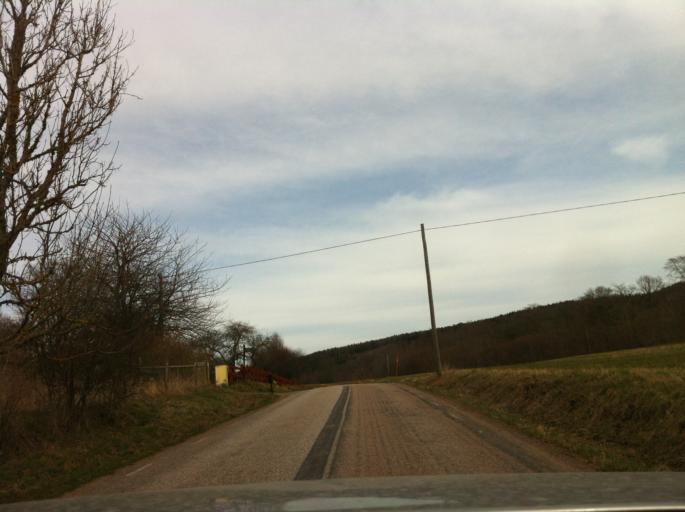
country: SE
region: Vaestra Goetaland
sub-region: Skara Kommun
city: Axvall
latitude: 58.4168
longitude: 13.6754
